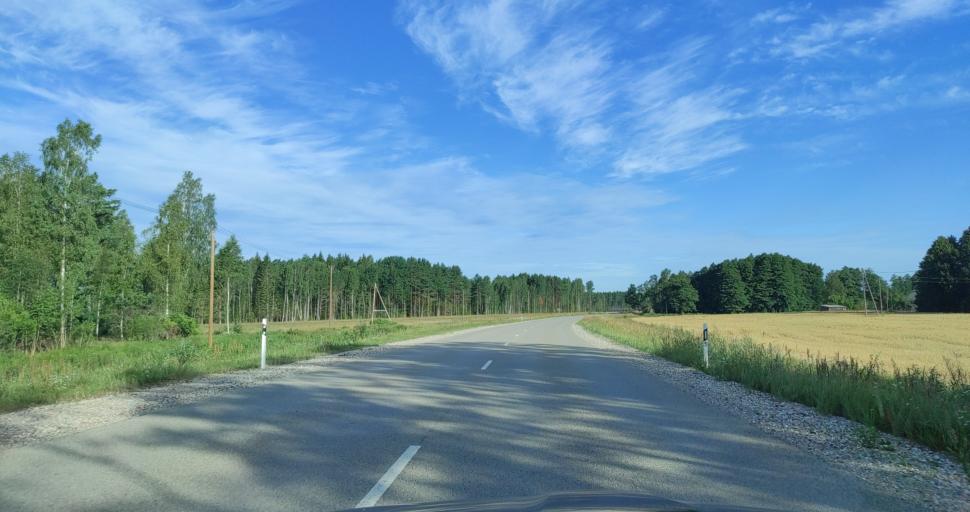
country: LV
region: Pavilostas
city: Pavilosta
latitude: 56.7957
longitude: 21.2352
